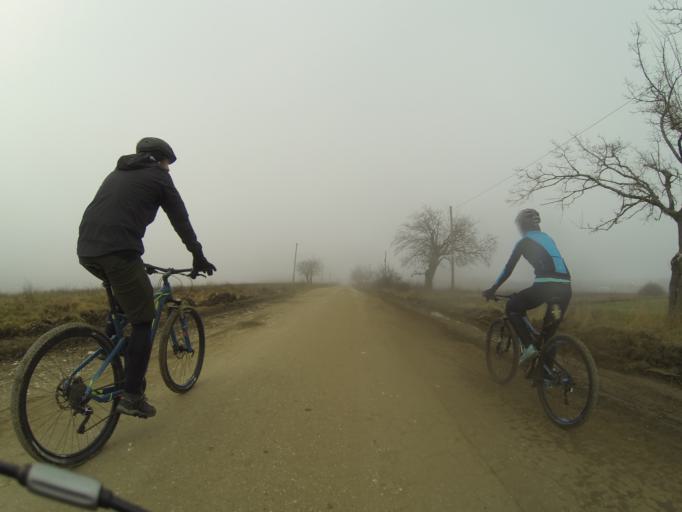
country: RO
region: Mehedinti
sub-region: Comuna Baclesu
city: Baclesu
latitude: 44.4839
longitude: 23.1031
